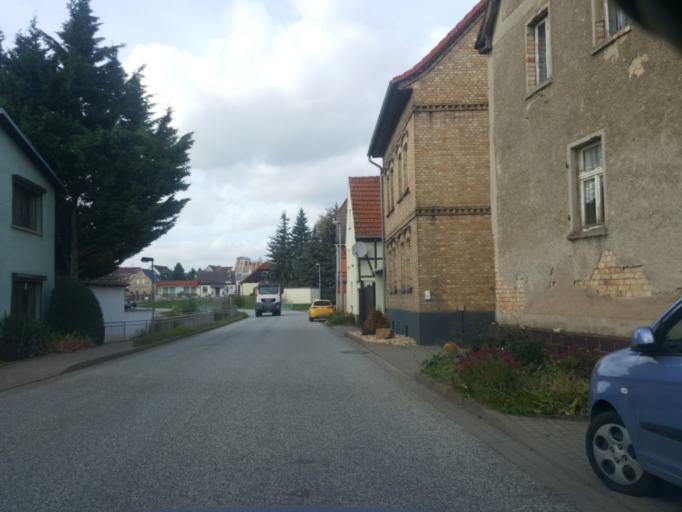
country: DE
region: Saxony-Anhalt
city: Riestedt
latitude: 51.4953
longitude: 11.3630
